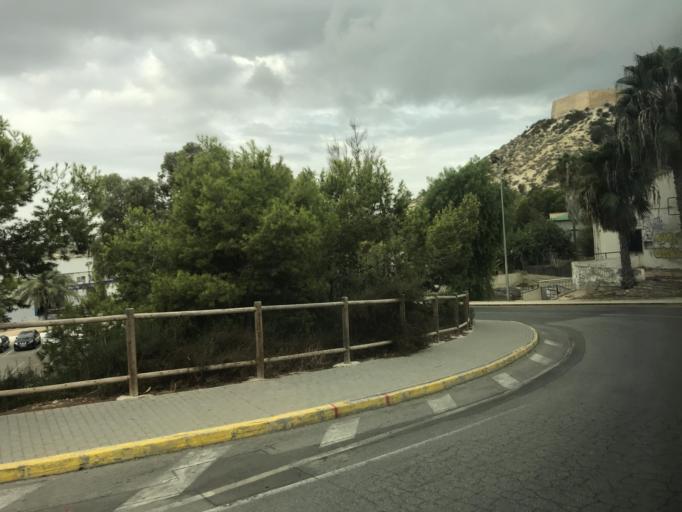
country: ES
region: Valencia
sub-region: Provincia de Alicante
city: Guardamar del Segura
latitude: 38.0889
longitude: -0.6559
